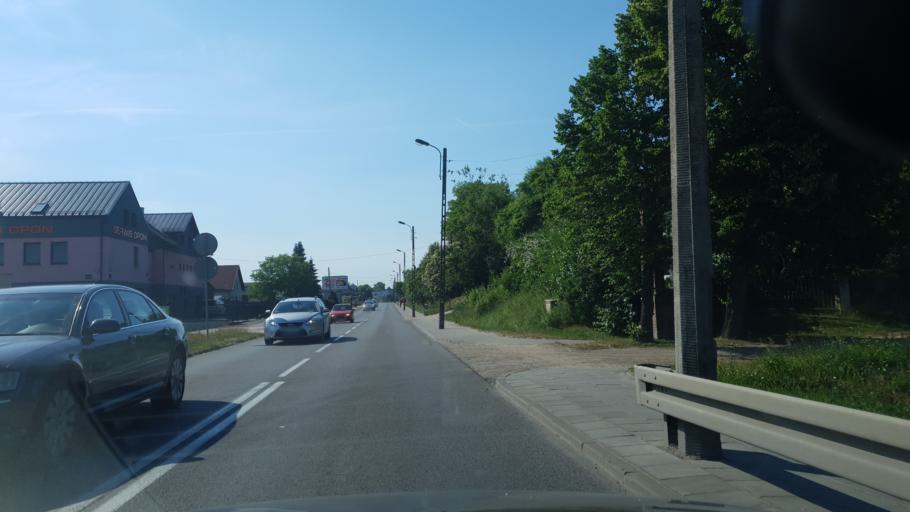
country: PL
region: Pomeranian Voivodeship
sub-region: Gdynia
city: Wielki Kack
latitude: 54.4384
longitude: 18.4613
